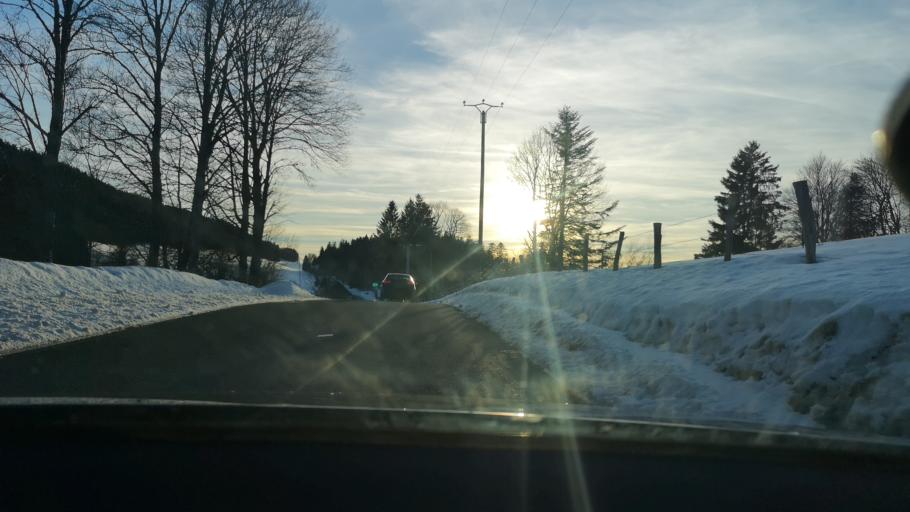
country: FR
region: Franche-Comte
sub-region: Departement du Doubs
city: Gilley
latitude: 46.9831
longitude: 6.5025
